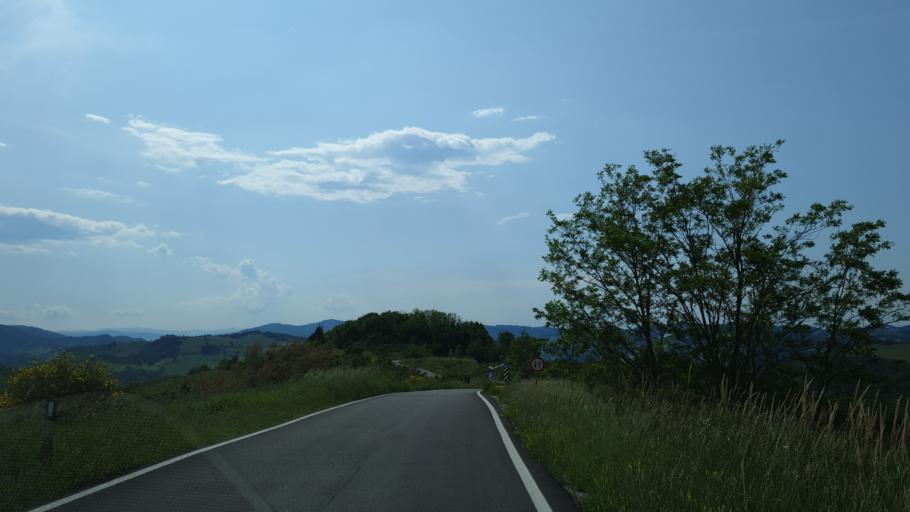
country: IT
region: Emilia-Romagna
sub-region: Provincia di Rimini
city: Sant'Agata Feltria
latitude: 43.9086
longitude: 12.2177
